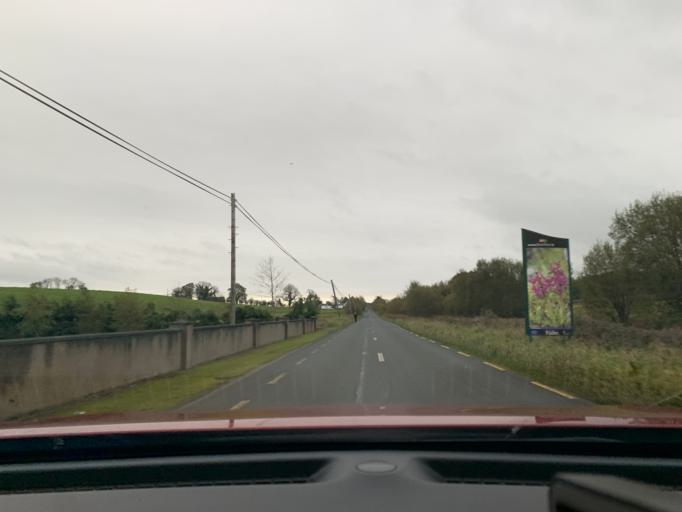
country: IE
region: Connaught
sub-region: Sligo
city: Ballymote
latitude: 54.0768
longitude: -8.5144
